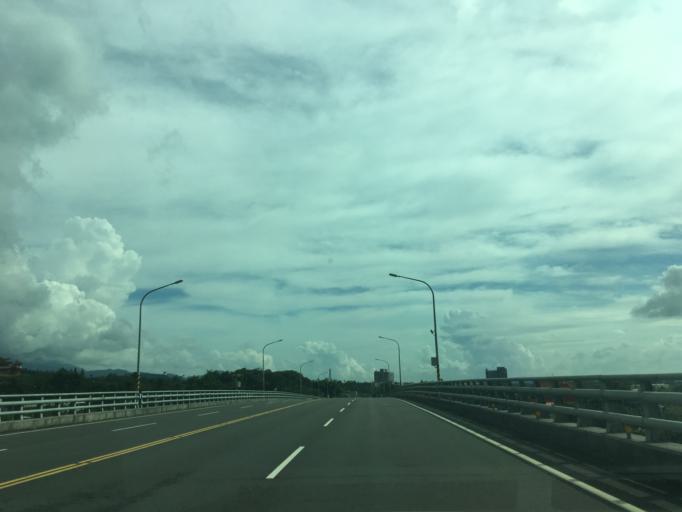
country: TW
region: Taiwan
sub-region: Chiayi
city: Jiayi Shi
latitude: 23.4518
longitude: 120.5512
